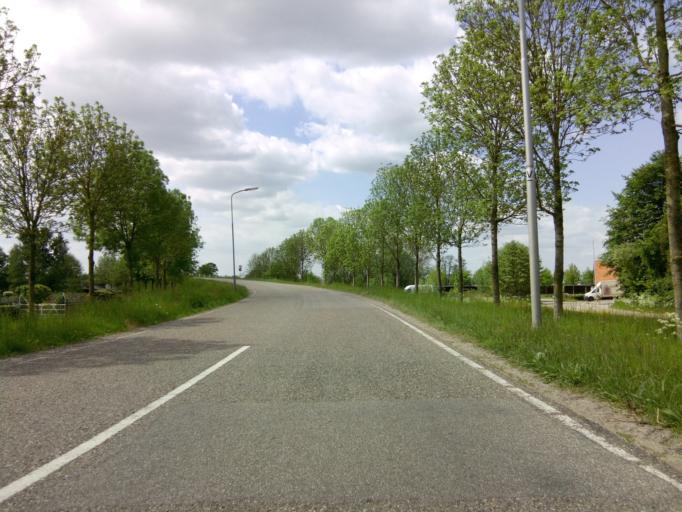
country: NL
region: Gelderland
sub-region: Gemeente Ede
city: Lunteren
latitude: 52.0682
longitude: 5.6102
